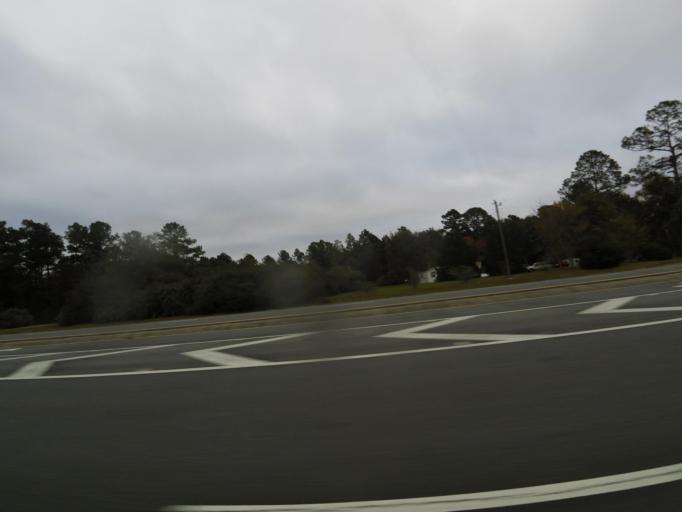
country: US
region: Georgia
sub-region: Charlton County
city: Folkston
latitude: 30.9096
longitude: -82.0745
